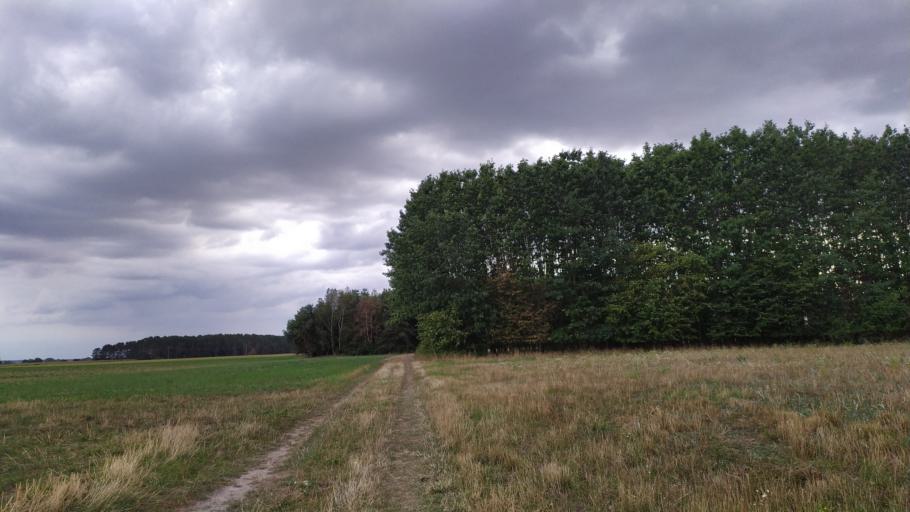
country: DE
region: Mecklenburg-Vorpommern
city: Wolgast
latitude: 54.0478
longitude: 13.8095
